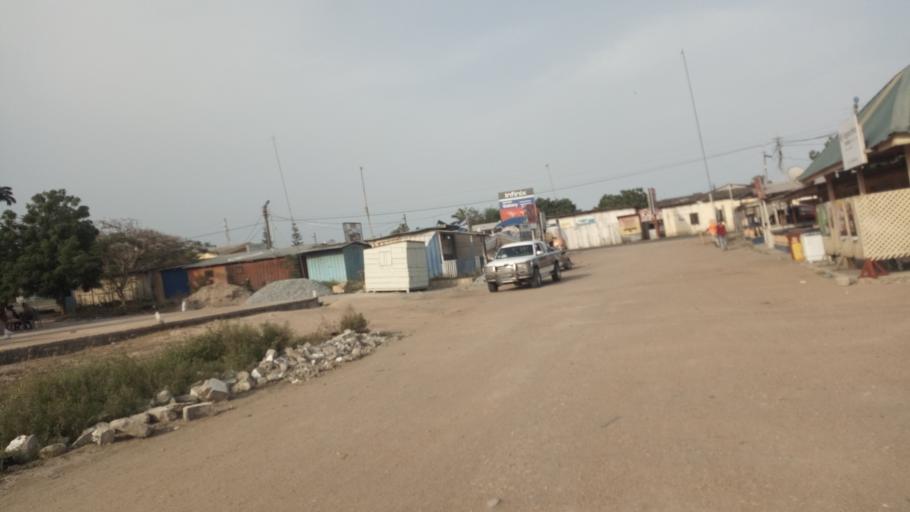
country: GH
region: Central
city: Winneba
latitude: 5.3521
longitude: -0.6312
